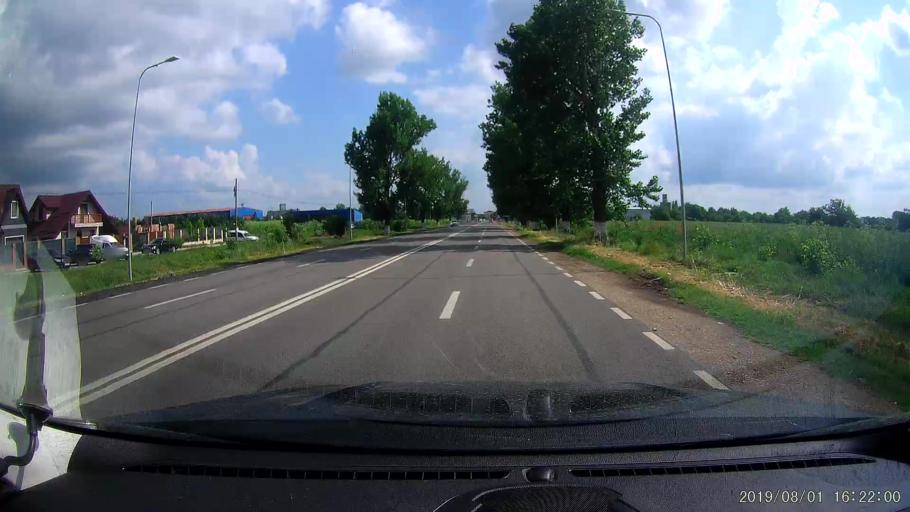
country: RO
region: Calarasi
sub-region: Municipiul Calarasi
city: Calarasi
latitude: 44.2091
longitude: 27.3385
